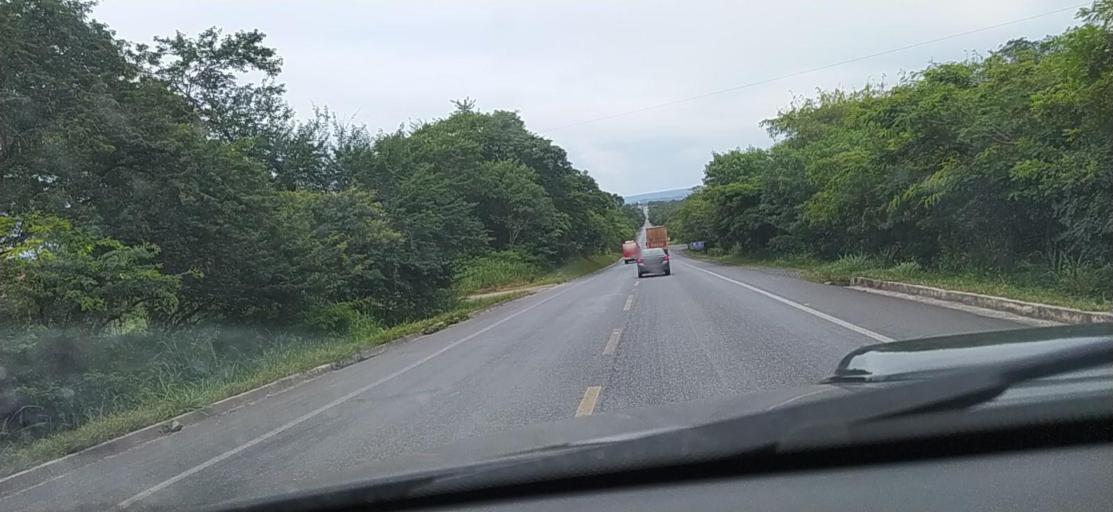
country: BR
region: Minas Gerais
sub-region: Montes Claros
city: Montes Claros
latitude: -16.6616
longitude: -43.7605
